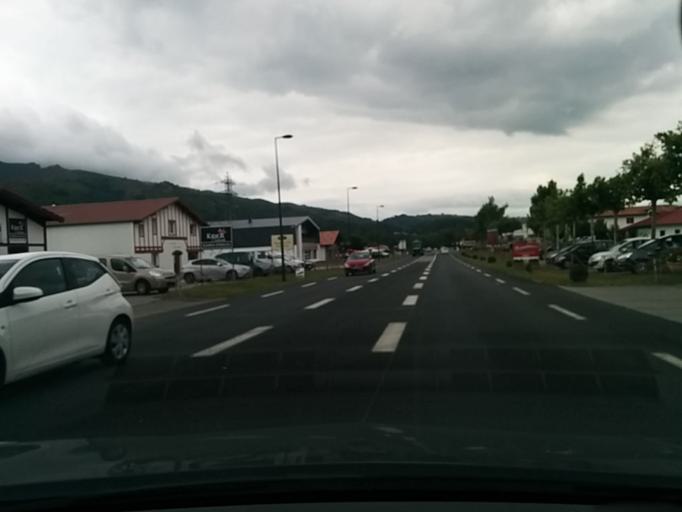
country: FR
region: Aquitaine
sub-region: Departement des Pyrenees-Atlantiques
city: Saint-Etienne-de-Baigorry
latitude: 43.2322
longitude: -1.2993
